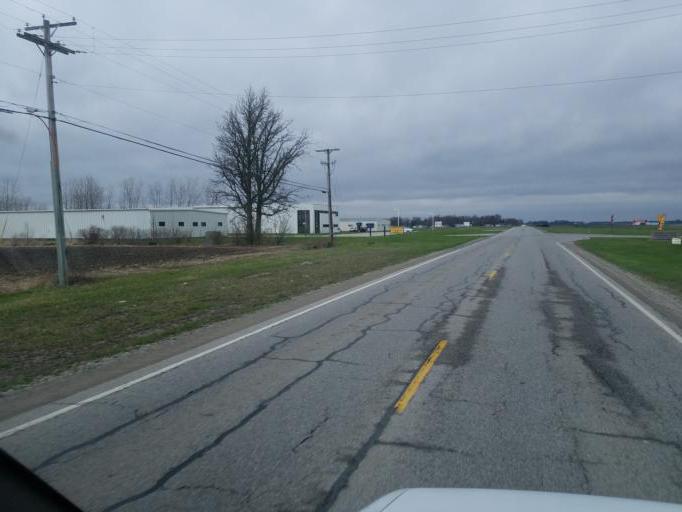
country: US
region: Ohio
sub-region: Marion County
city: Marion
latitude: 40.6071
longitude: -83.0735
